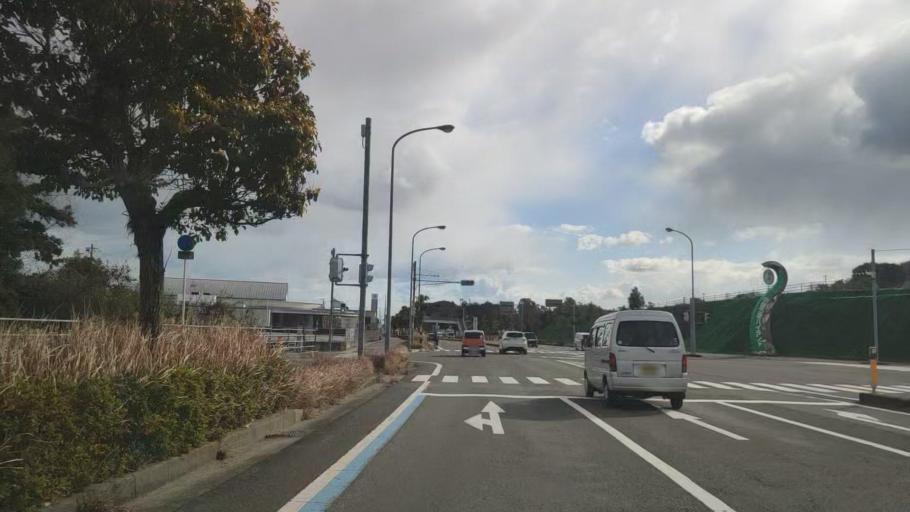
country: JP
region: Ehime
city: Hojo
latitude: 34.0632
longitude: 132.9548
